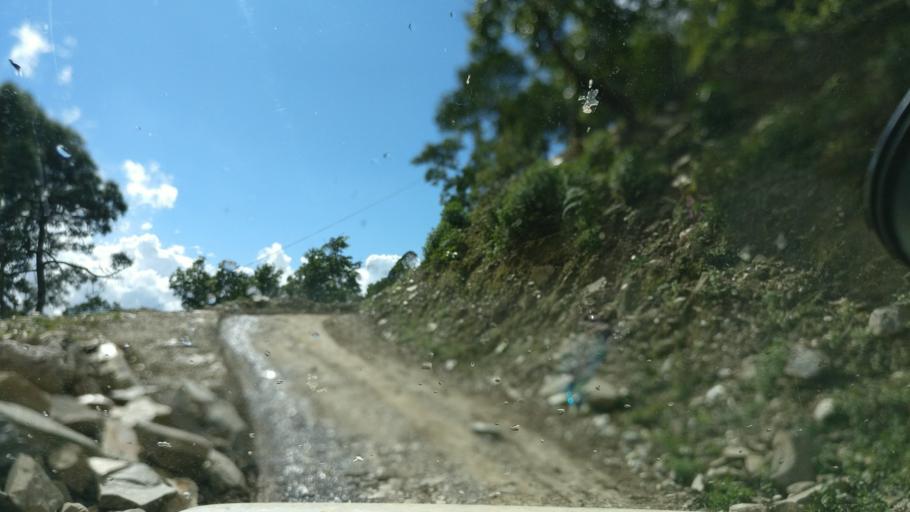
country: NP
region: Western Region
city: Baglung
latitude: 28.2756
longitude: 83.6425
